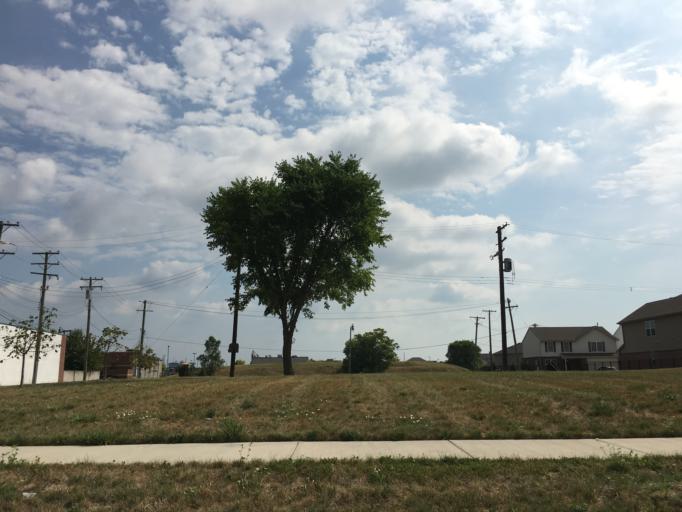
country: US
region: Michigan
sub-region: Wayne County
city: Grosse Pointe Park
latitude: 42.3637
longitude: -82.9760
